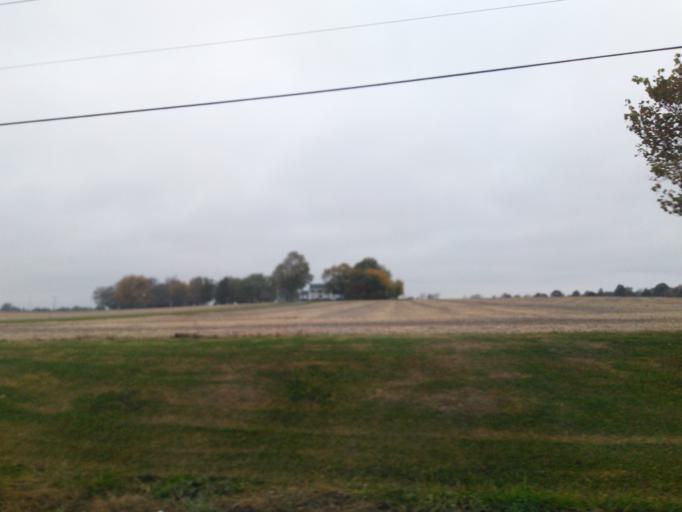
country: US
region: Illinois
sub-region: Bond County
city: Greenville
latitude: 38.8778
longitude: -89.4143
